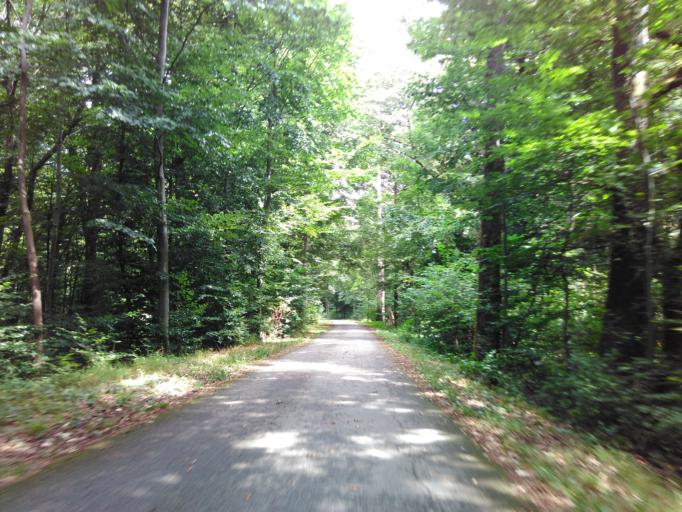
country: LU
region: Luxembourg
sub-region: Canton de Luxembourg
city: Sandweiler
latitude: 49.6471
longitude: 6.2204
